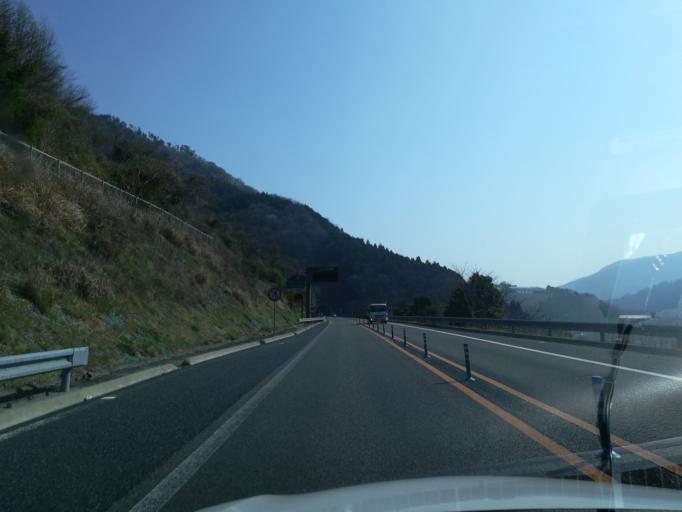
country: JP
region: Tokushima
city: Ikedacho
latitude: 34.0146
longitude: 133.7499
